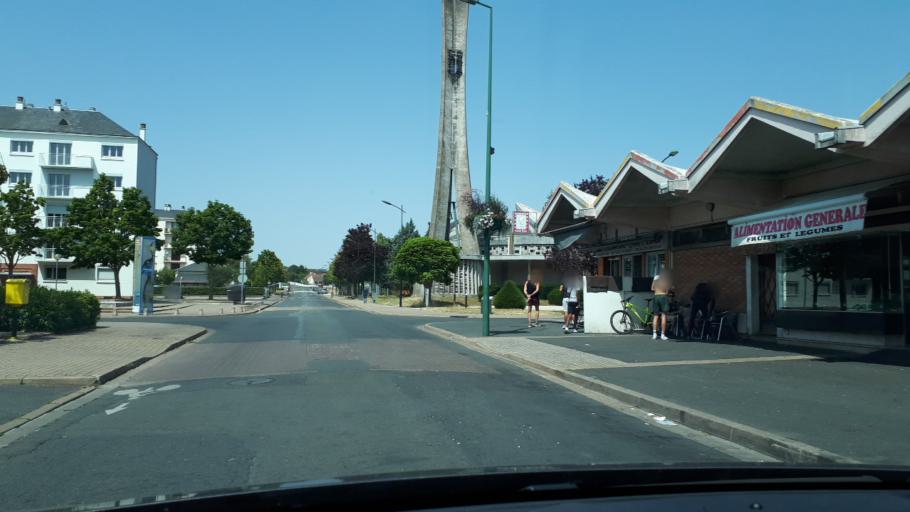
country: FR
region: Centre
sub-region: Departement du Loir-et-Cher
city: Vendome
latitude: 47.8069
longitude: 1.0658
